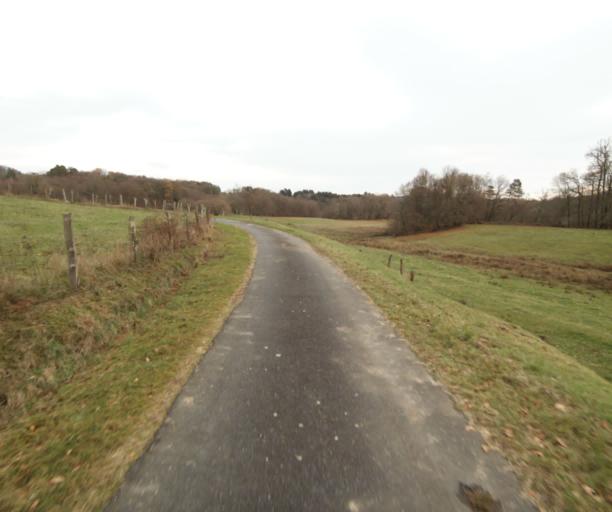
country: FR
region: Limousin
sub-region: Departement de la Correze
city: Chameyrat
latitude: 45.2412
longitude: 1.6817
